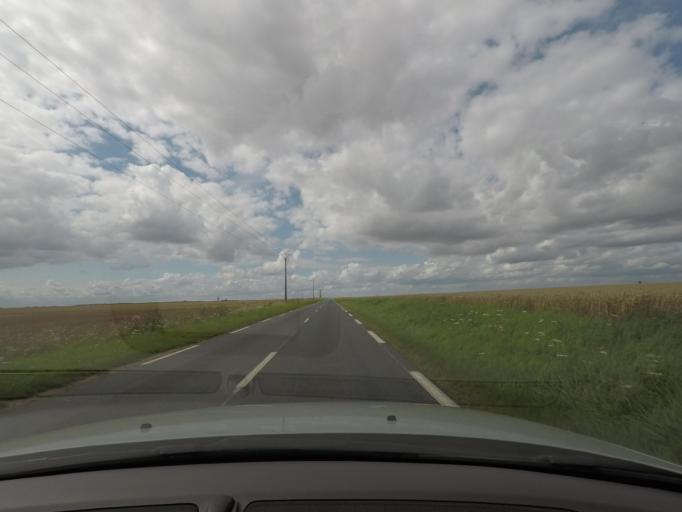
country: FR
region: Haute-Normandie
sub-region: Departement de l'Eure
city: Les Andelys
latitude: 49.2199
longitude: 1.4498
